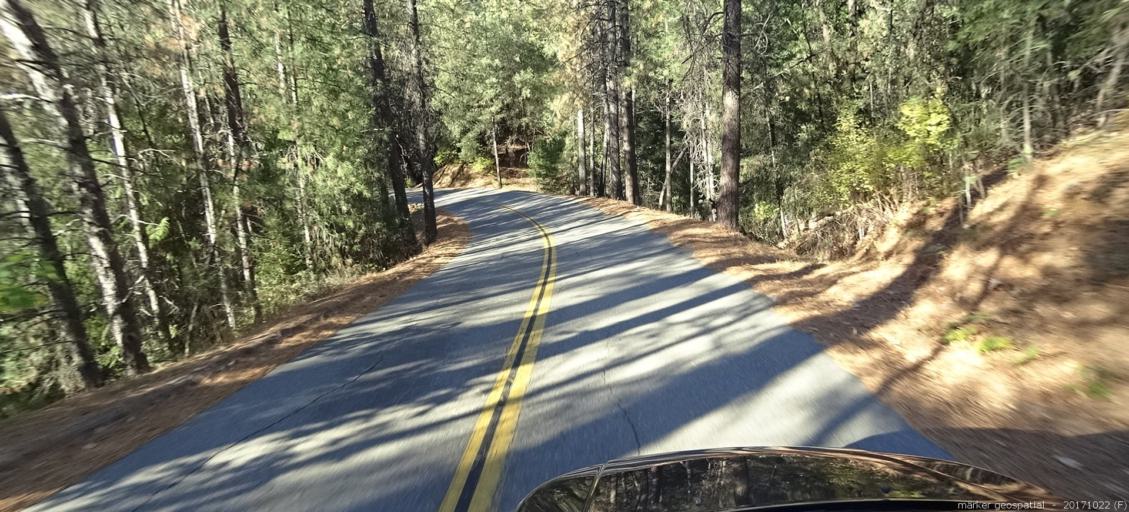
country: US
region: California
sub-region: Shasta County
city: Shasta Lake
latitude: 40.8735
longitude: -122.2533
